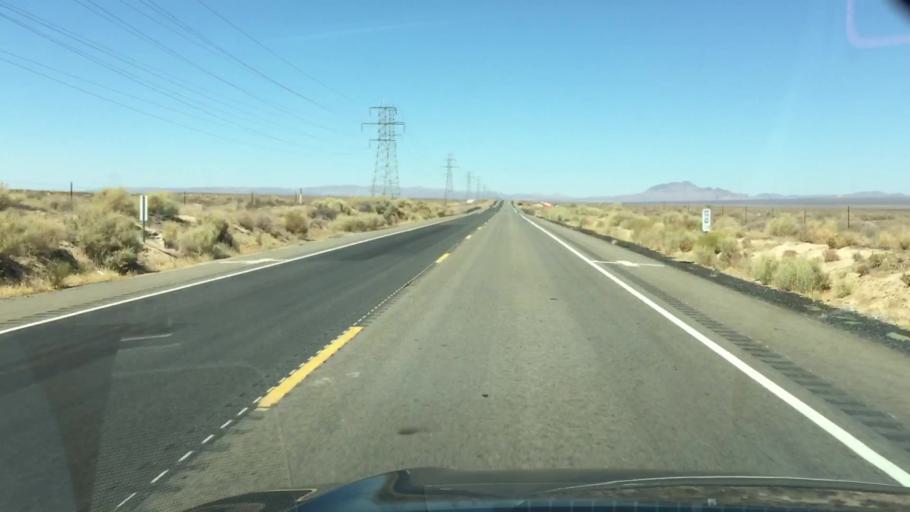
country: US
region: California
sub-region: Kern County
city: Boron
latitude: 35.0989
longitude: -117.5712
